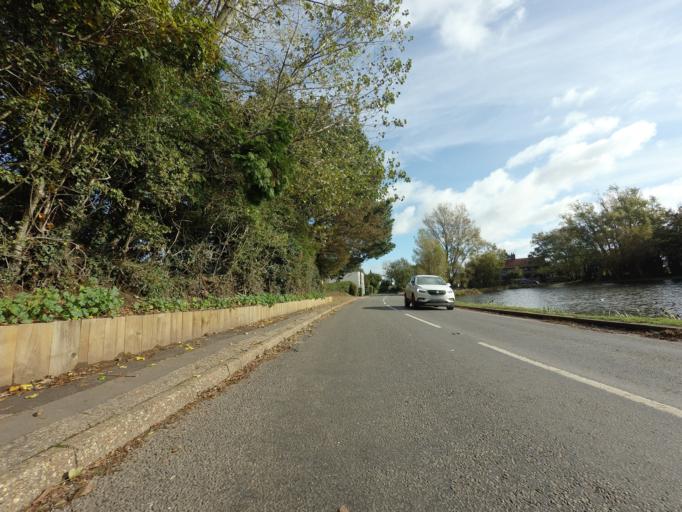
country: GB
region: England
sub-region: Norfolk
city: Wells-next-the-Sea
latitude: 52.9012
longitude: 0.6845
